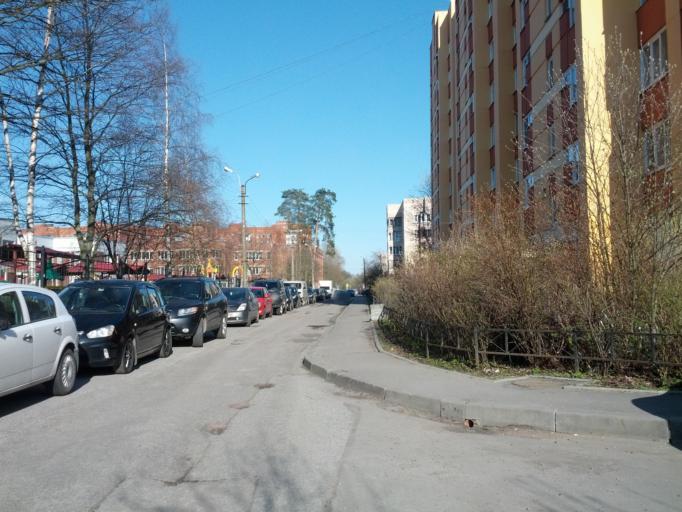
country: RU
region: St.-Petersburg
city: Sestroretsk
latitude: 60.0891
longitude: 29.9480
